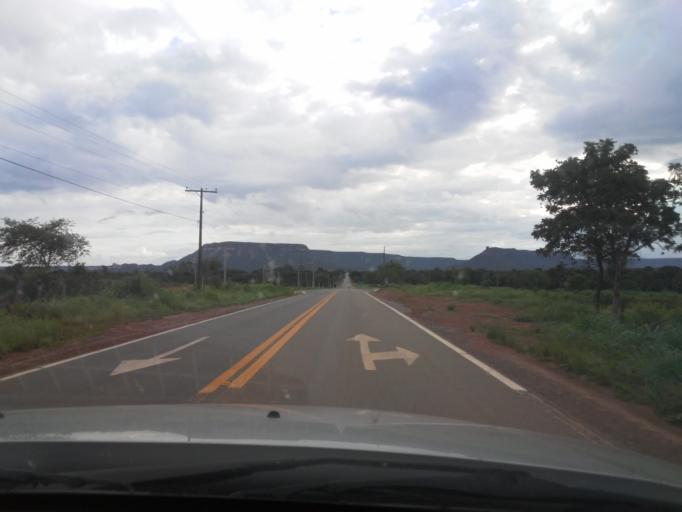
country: BR
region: Tocantins
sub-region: Taguatinga
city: Taguatinga
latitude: -12.3900
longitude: -46.4147
